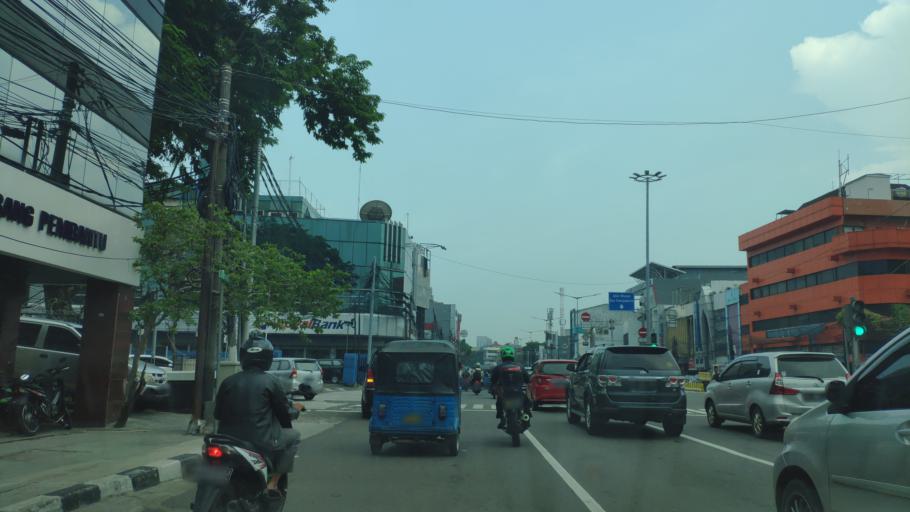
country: ID
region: Jakarta Raya
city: Jakarta
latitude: -6.1703
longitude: 106.8144
